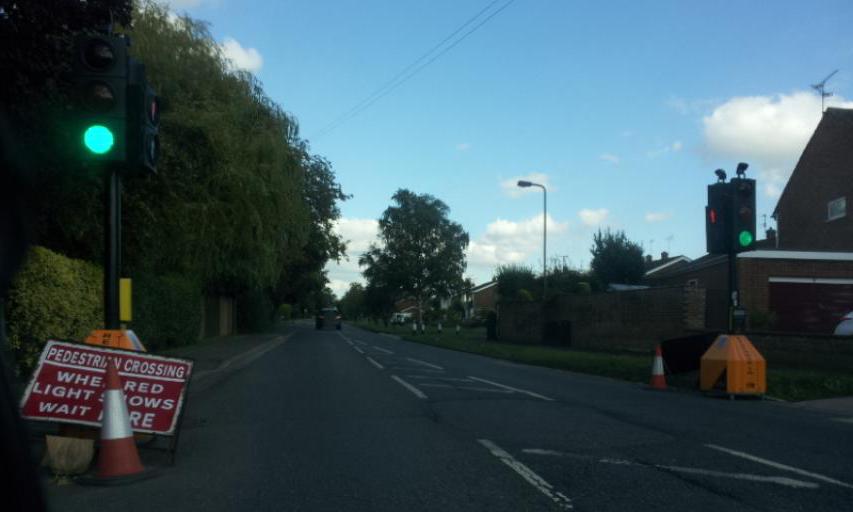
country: GB
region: England
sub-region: Kent
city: Staplehurst
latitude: 51.1651
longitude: 0.5476
